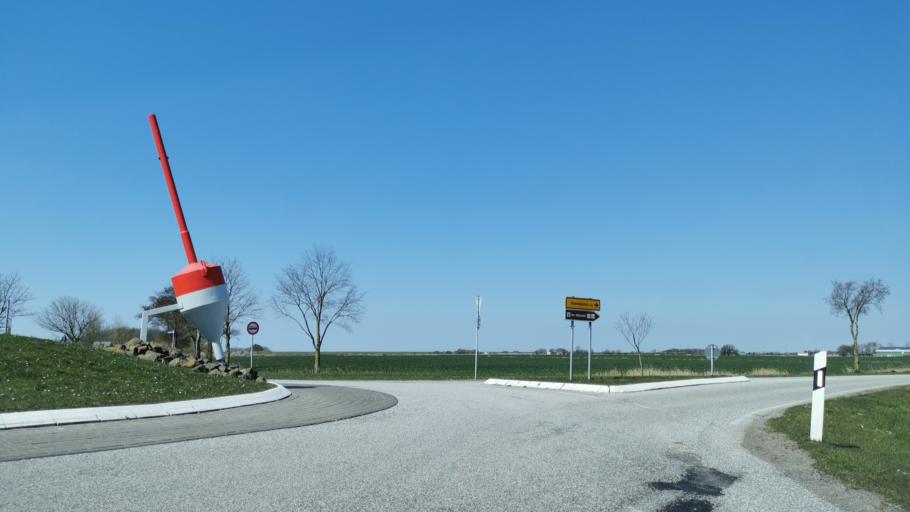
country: DE
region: Schleswig-Holstein
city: Busum
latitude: 54.1413
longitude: 8.8520
